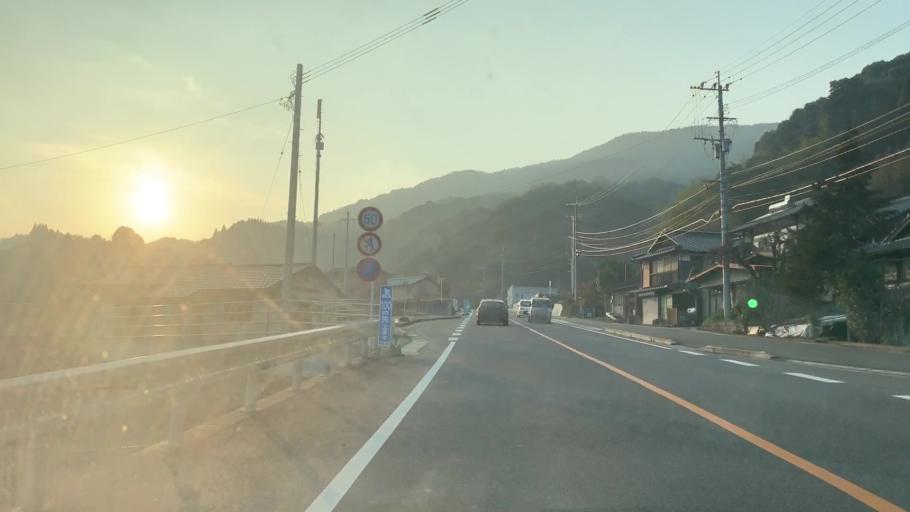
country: JP
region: Saga Prefecture
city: Takeocho-takeo
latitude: 33.2629
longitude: 130.0340
